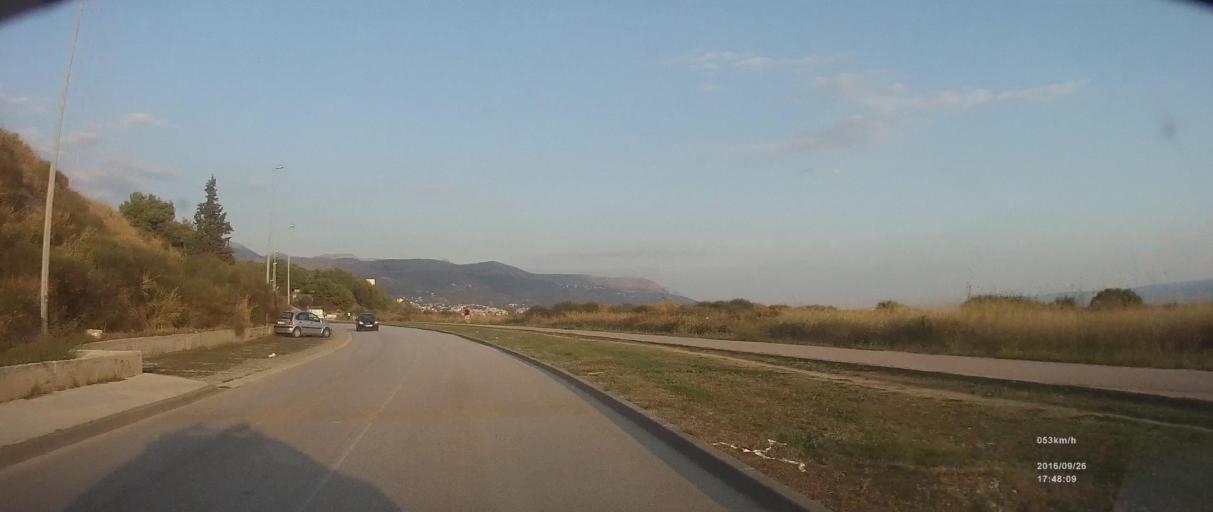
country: HR
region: Splitsko-Dalmatinska
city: Kamen
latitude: 43.5017
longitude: 16.4889
